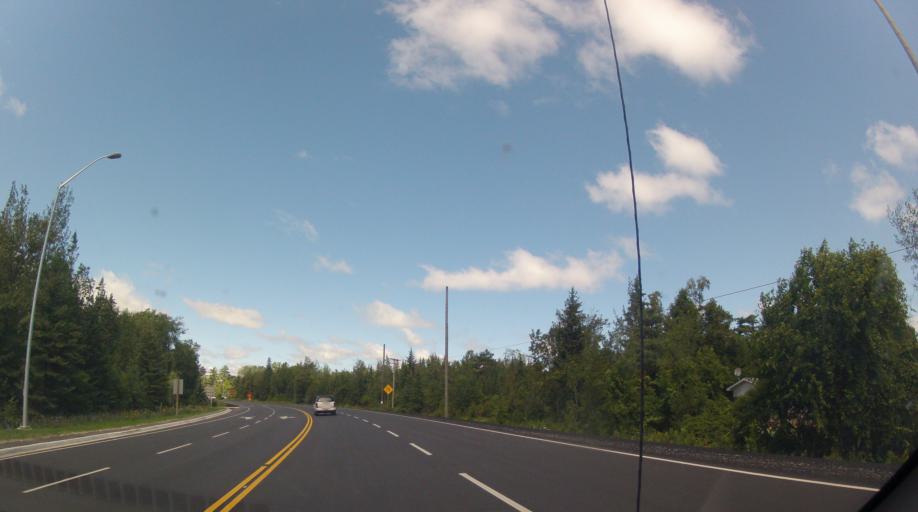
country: CA
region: Ontario
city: Wasaga Beach
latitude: 44.4676
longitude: -80.1090
